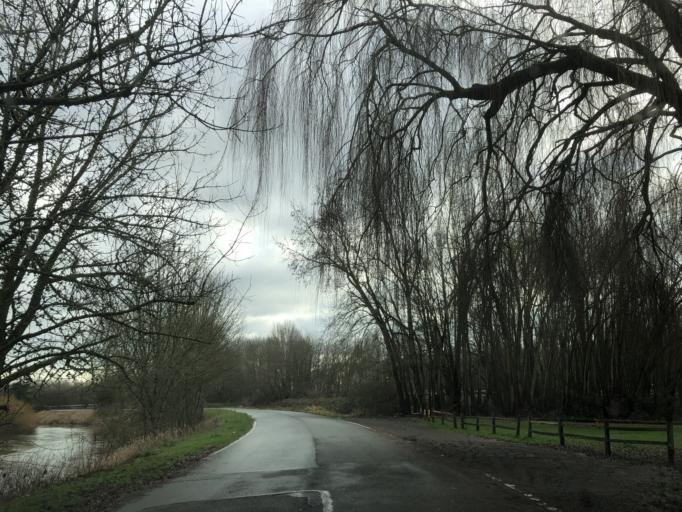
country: US
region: Washington
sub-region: King County
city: Kent
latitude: 47.3772
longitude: -122.2686
